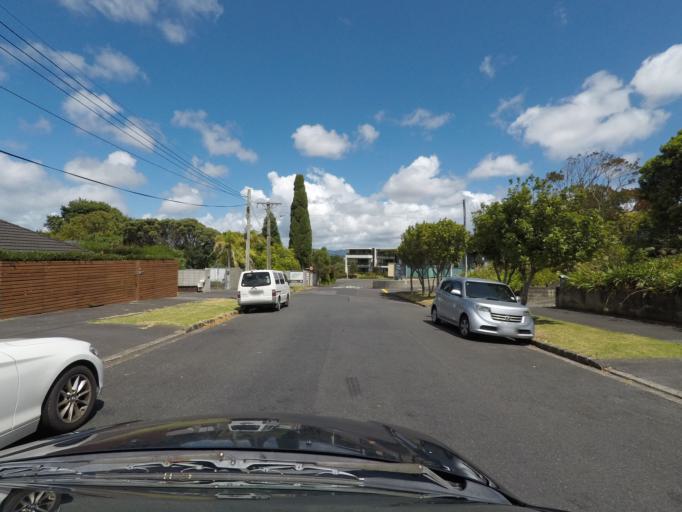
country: NZ
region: Auckland
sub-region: Auckland
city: Rosebank
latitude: -36.8666
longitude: 174.6995
